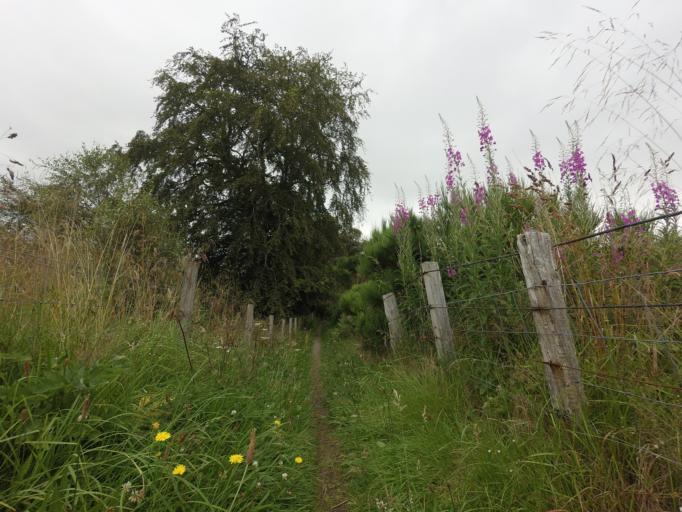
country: GB
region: Scotland
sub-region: Highland
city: Evanton
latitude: 57.9228
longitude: -4.4033
